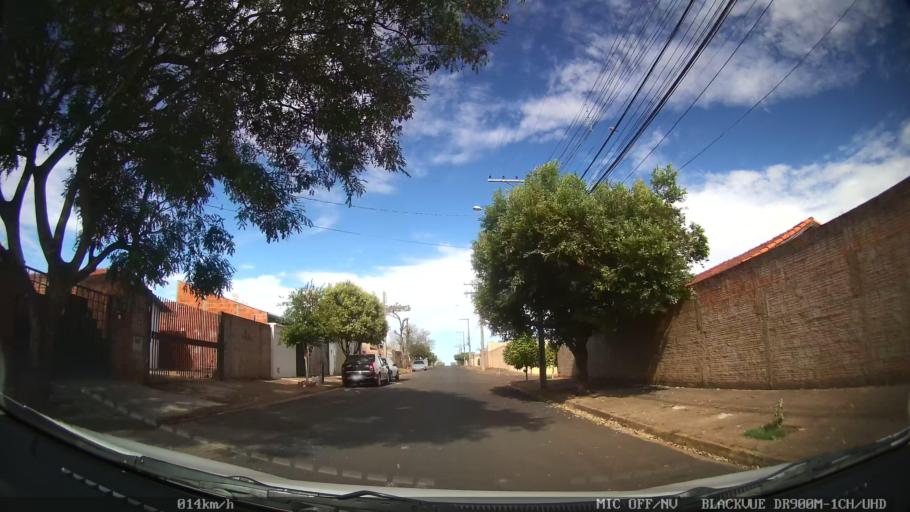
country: BR
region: Sao Paulo
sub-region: Catanduva
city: Catanduva
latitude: -21.1256
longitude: -48.9403
